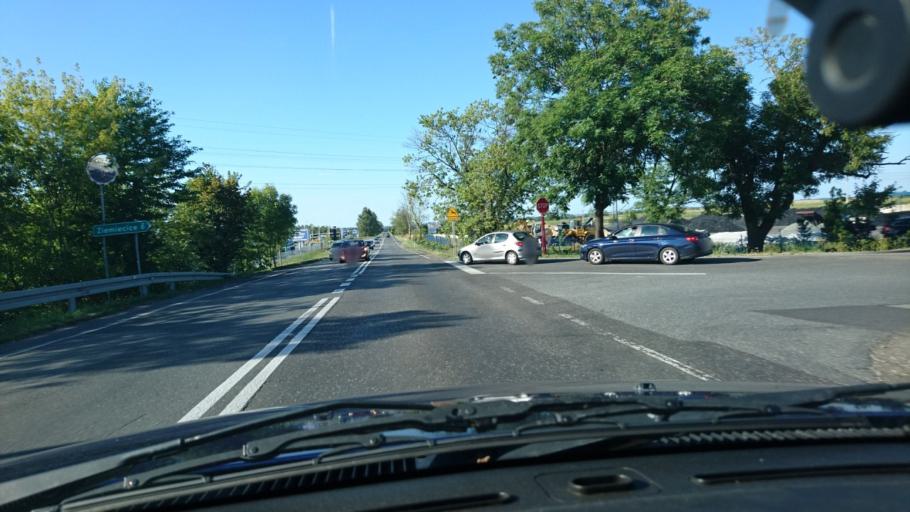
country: PL
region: Silesian Voivodeship
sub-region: Powiat gliwicki
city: Pyskowice
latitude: 50.3741
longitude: 18.6348
